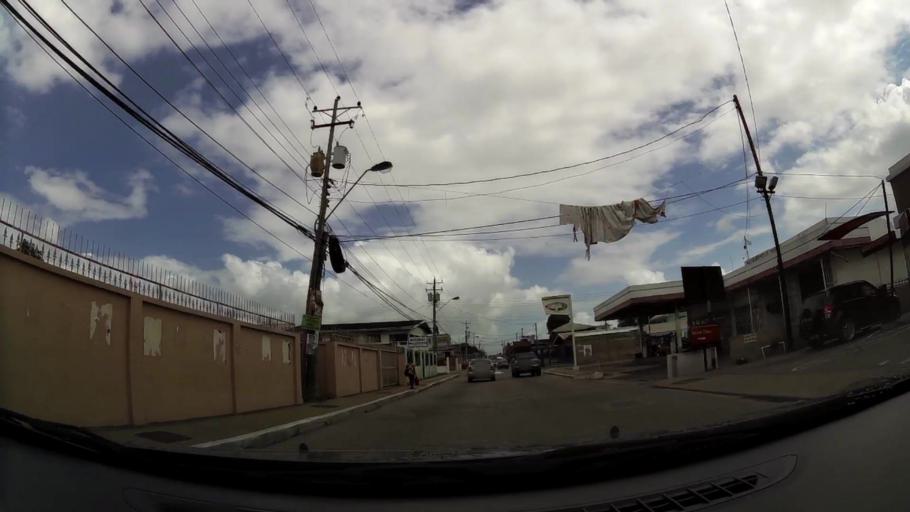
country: TT
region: Tunapuna/Piarco
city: Arouca
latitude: 10.6337
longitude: -61.3388
